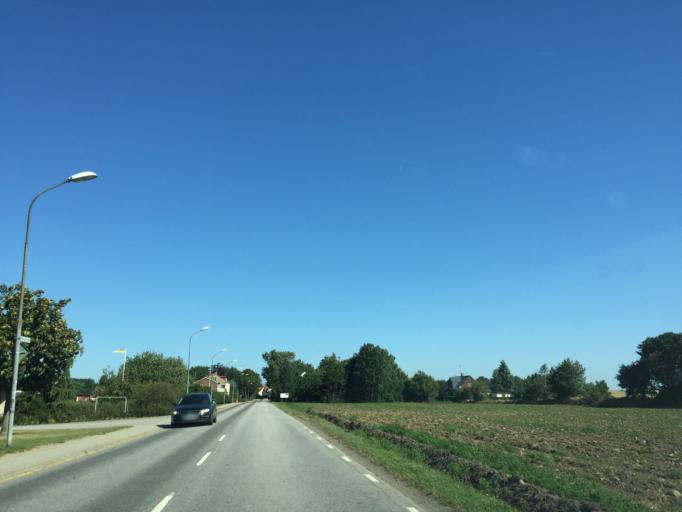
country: SE
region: Skane
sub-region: Ystads Kommun
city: Kopingebro
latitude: 55.4334
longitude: 14.1134
